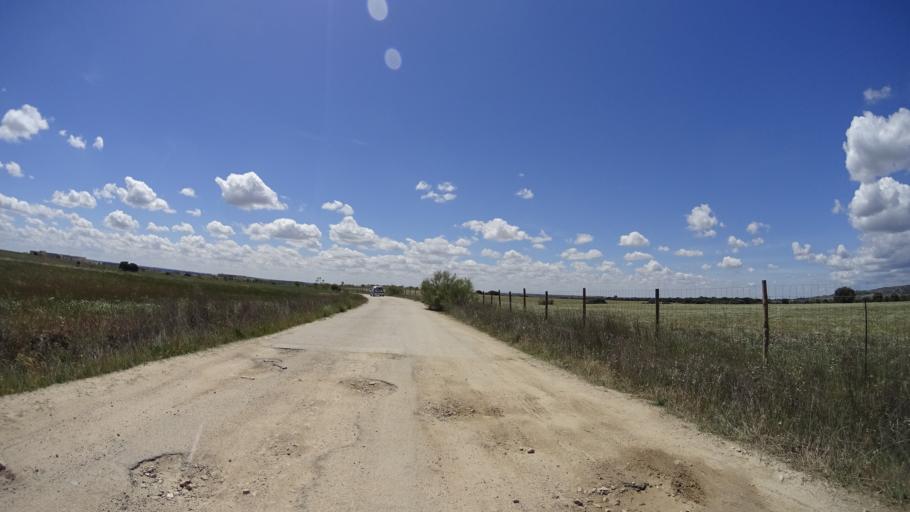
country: ES
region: Madrid
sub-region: Provincia de Madrid
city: Villanueva del Pardillo
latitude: 40.4966
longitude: -3.9920
